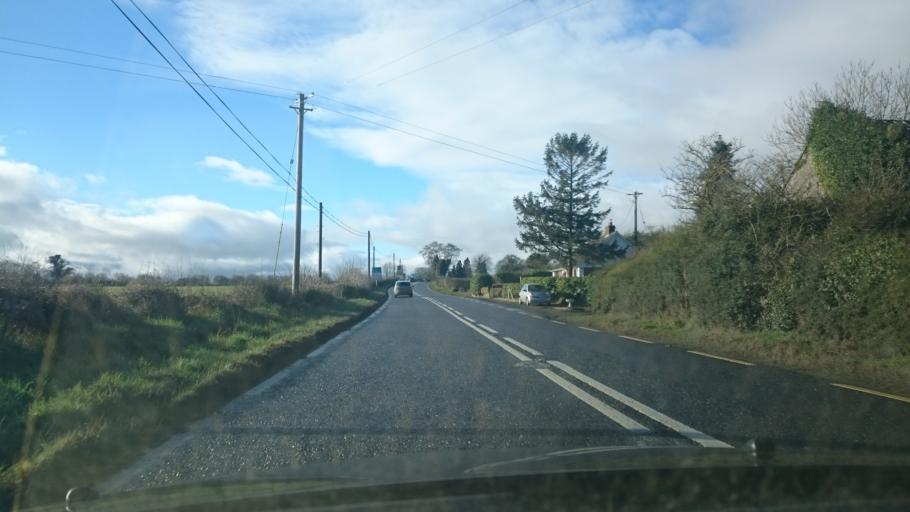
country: IE
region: Leinster
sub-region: Kilkenny
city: Callan
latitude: 52.5771
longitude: -7.3253
